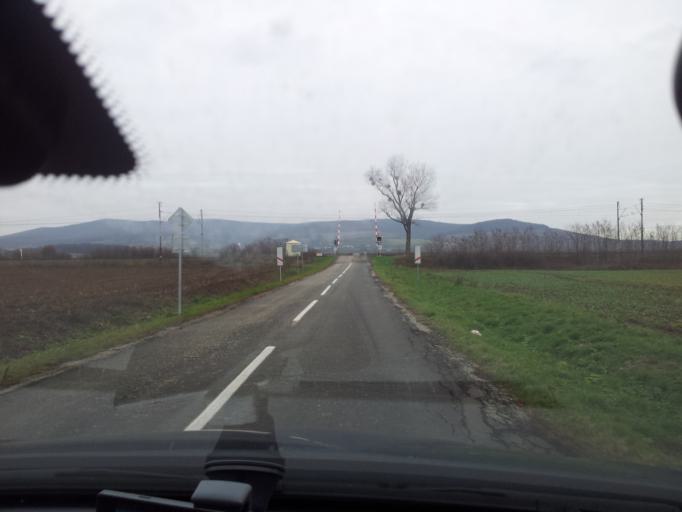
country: HU
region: Borsod-Abauj-Zemplen
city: Satoraljaujhely
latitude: 48.4455
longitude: 21.6537
